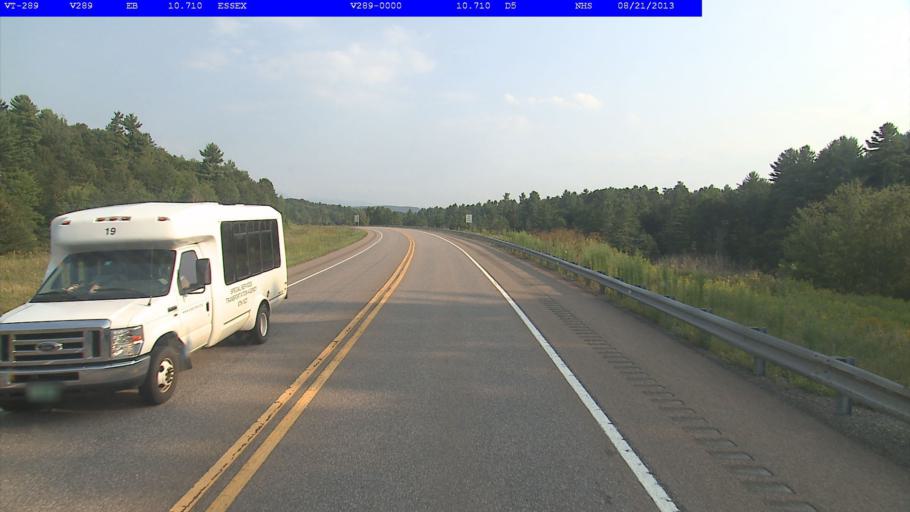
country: US
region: Vermont
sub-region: Chittenden County
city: Essex Junction
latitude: 44.4970
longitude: -73.0692
